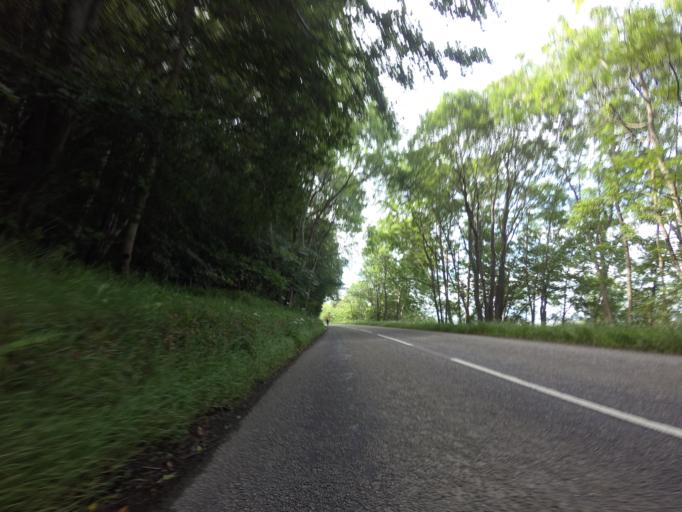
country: GB
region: Scotland
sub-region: Highland
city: Tain
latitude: 57.8278
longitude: -4.1304
